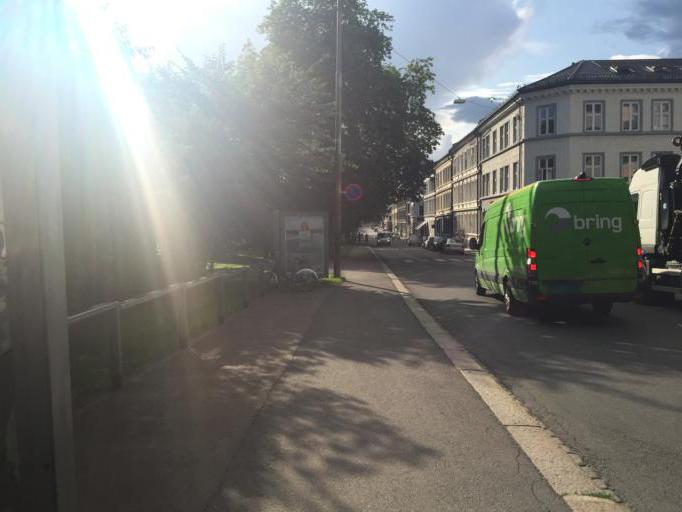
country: NO
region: Oslo
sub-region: Oslo
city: Oslo
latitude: 59.9232
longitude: 10.7665
